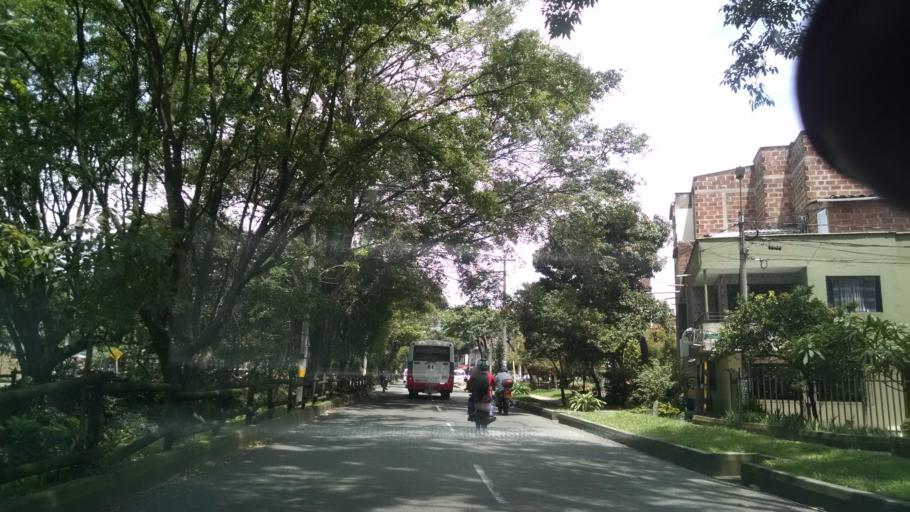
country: CO
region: Antioquia
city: Itagui
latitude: 6.2137
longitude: -75.5864
